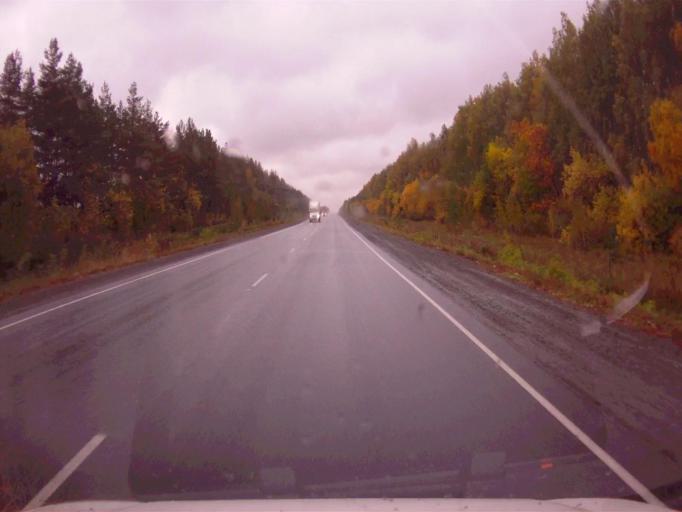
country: RU
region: Chelyabinsk
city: Roshchino
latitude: 55.3751
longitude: 61.1515
